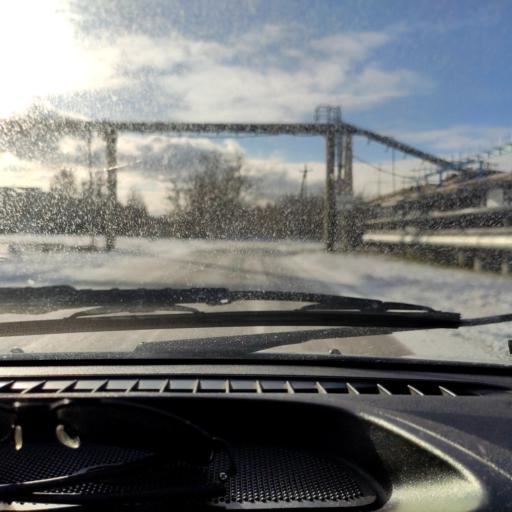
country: RU
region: Samara
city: Zhigulevsk
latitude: 53.5345
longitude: 49.4818
